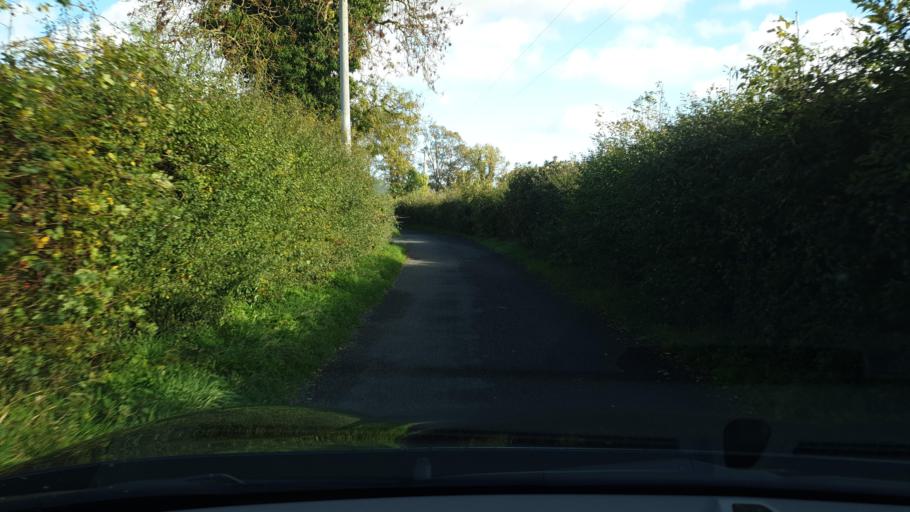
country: IE
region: Leinster
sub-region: Fingal County
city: Swords
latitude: 53.4916
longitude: -6.2555
